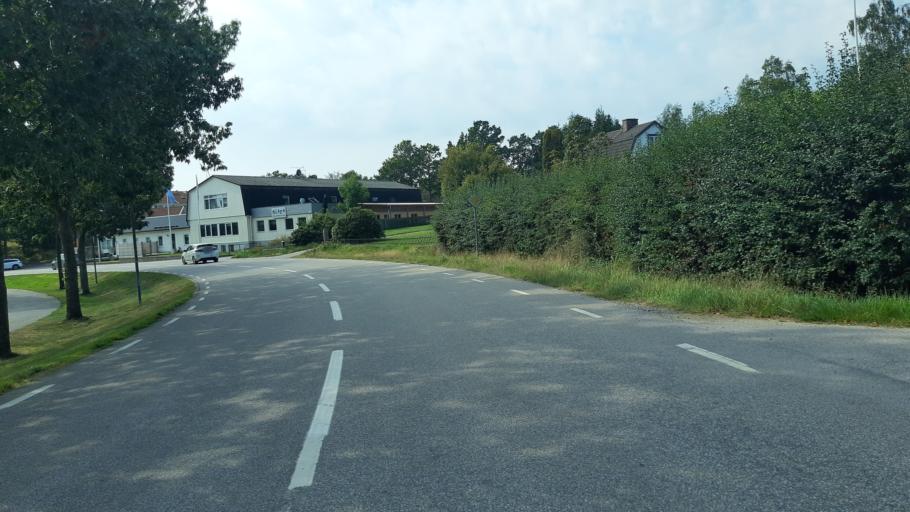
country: SE
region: Blekinge
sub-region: Karlskrona Kommun
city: Nattraby
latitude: 56.1920
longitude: 15.5310
